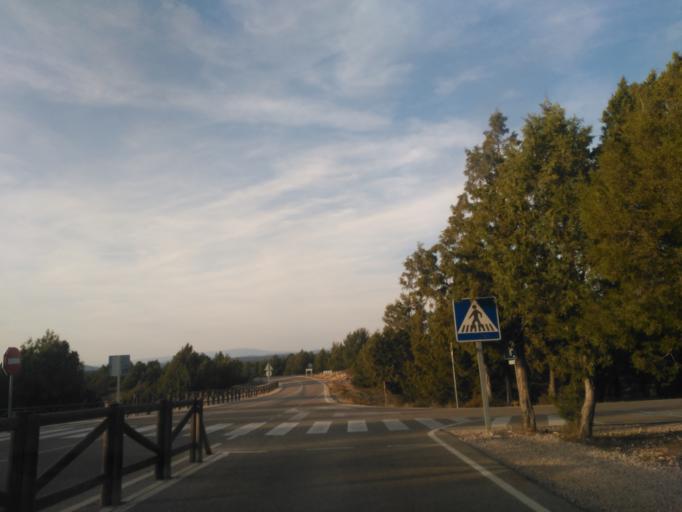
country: ES
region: Castille and Leon
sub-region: Provincia de Soria
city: Ucero
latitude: 41.7317
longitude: -3.0422
